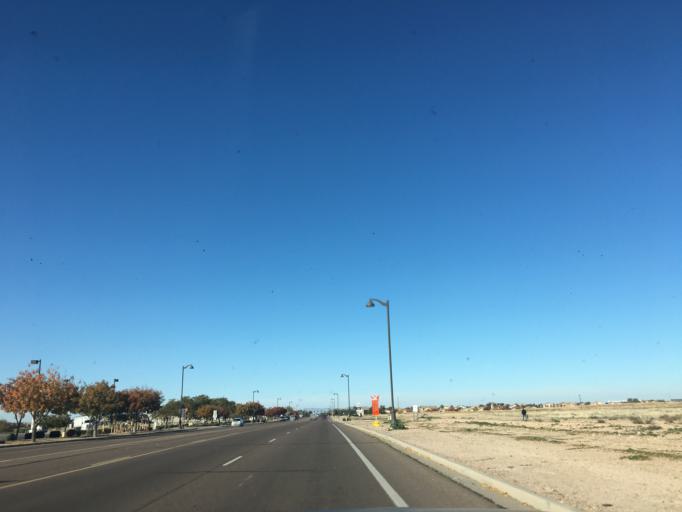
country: US
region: Arizona
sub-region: Pinal County
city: Maricopa
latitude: 33.0385
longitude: -112.0125
